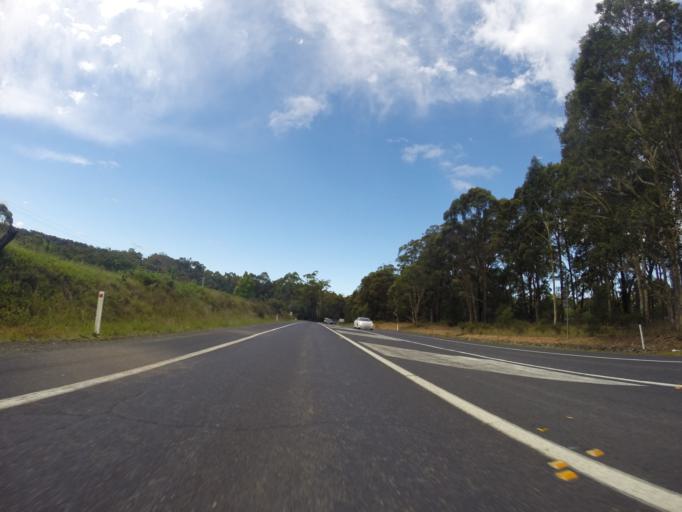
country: AU
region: New South Wales
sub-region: Shoalhaven Shire
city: Falls Creek
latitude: -35.0838
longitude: 150.5431
